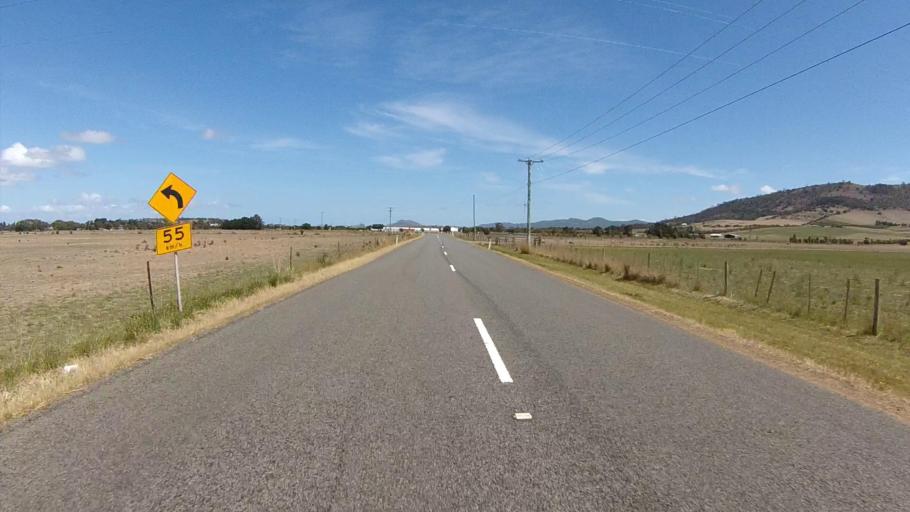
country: AU
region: Tasmania
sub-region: Sorell
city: Sorell
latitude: -42.7660
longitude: 147.5162
